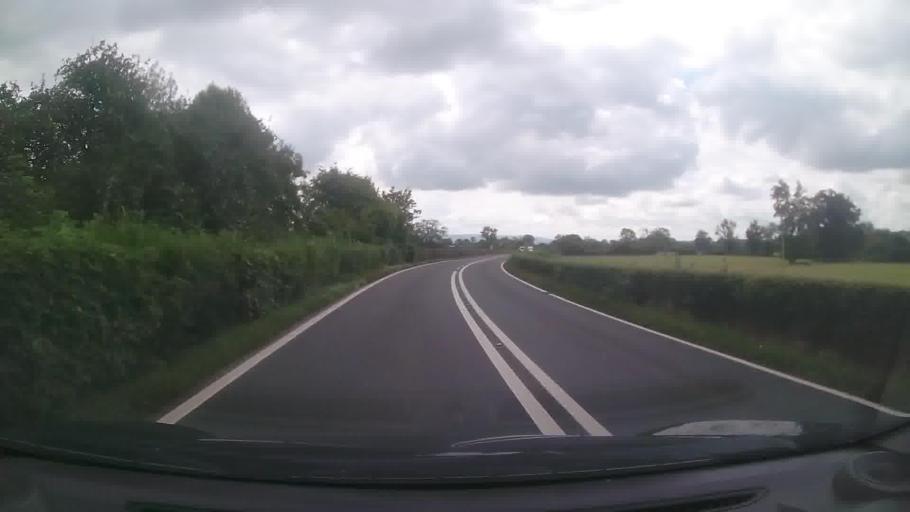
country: GB
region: England
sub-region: Shropshire
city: Pant
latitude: 52.7756
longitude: -3.0852
